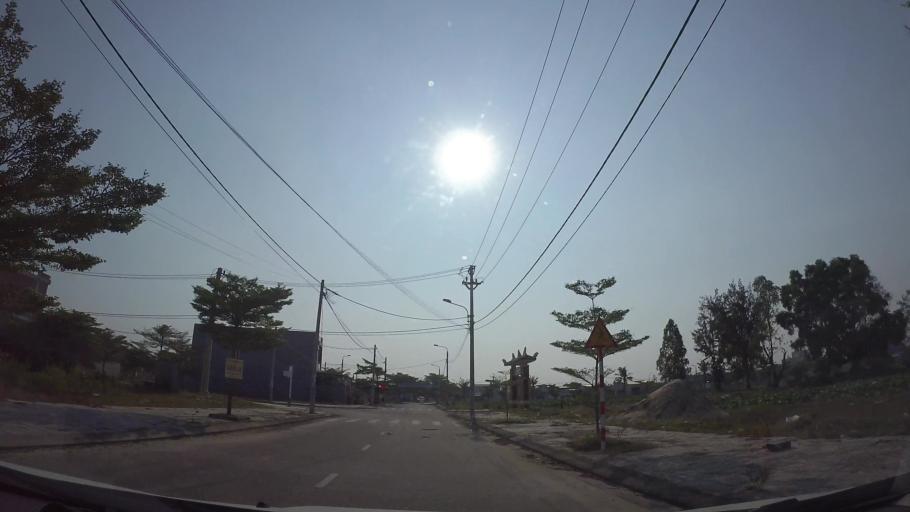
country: VN
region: Quang Nam
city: Quang Nam
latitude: 15.9478
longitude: 108.2613
